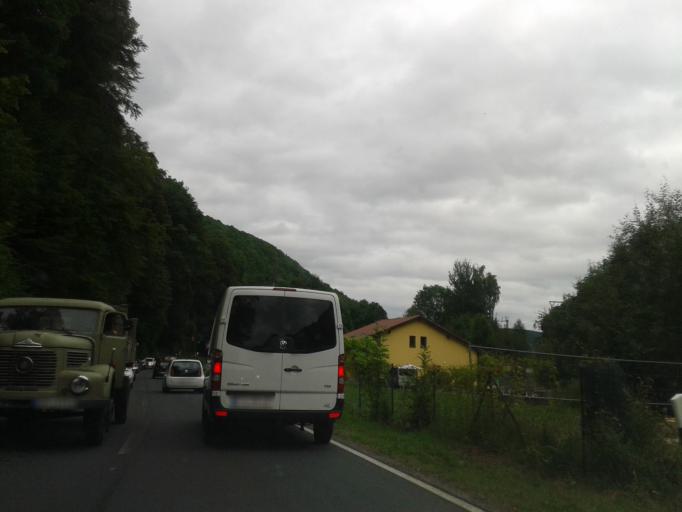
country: DE
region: Saxony
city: Tharandt
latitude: 50.9832
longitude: 13.6026
